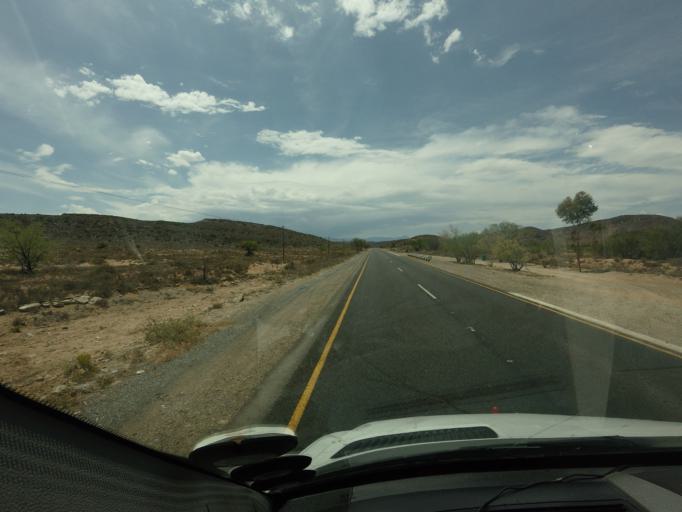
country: ZA
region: Western Cape
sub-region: Eden District Municipality
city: Ladismith
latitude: -33.7585
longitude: 20.9446
